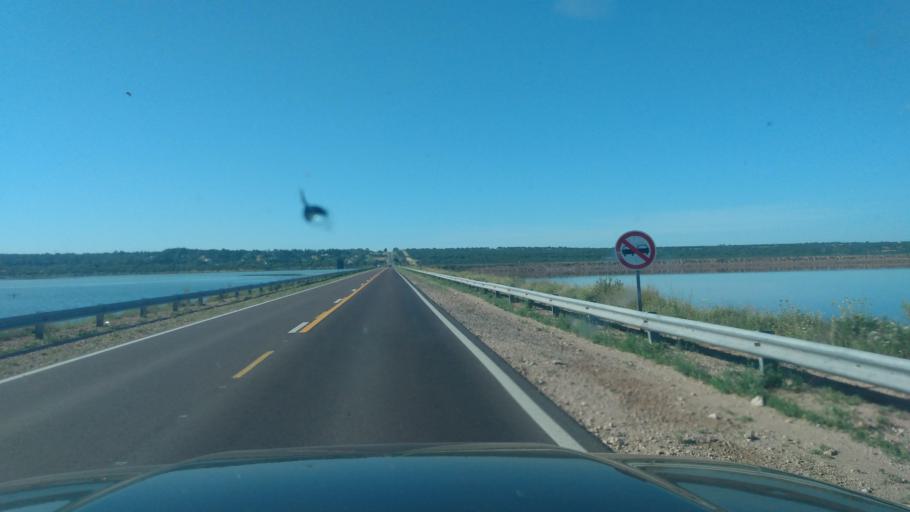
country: AR
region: La Pampa
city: Santa Rosa
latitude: -36.7099
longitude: -64.2831
